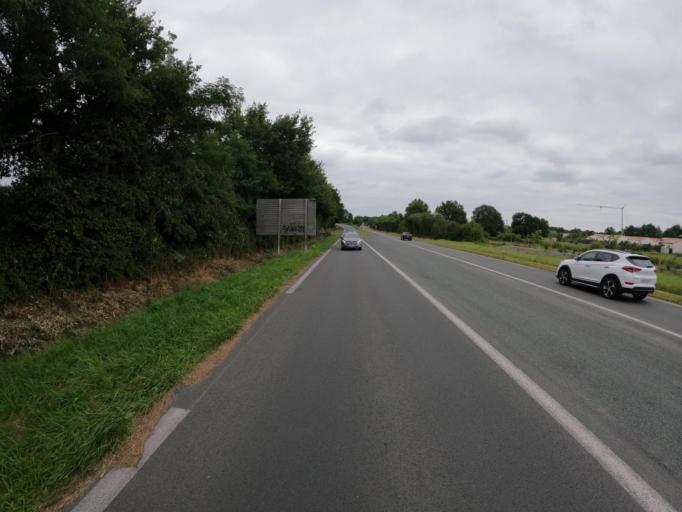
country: FR
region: Pays de la Loire
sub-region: Departement de la Vendee
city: Belleville-sur-Vie
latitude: 46.7730
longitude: -1.4307
